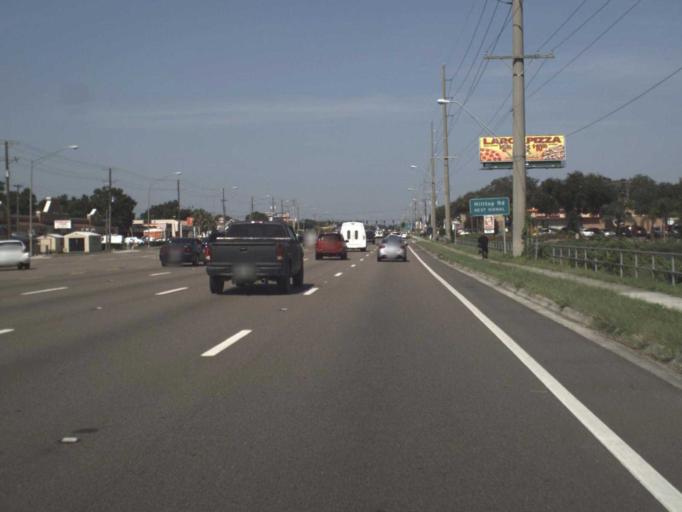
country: US
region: Florida
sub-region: Hillsborough County
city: Brandon
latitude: 27.9379
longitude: -82.3016
